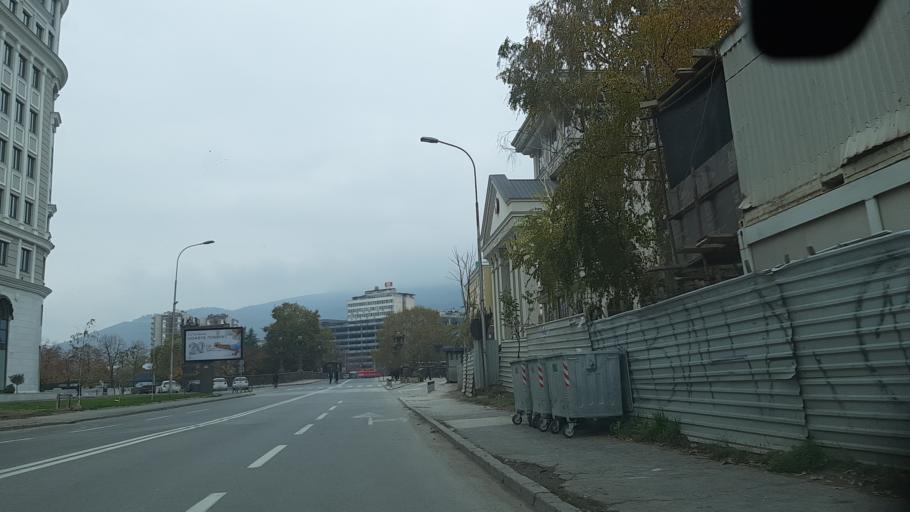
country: MK
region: Karpos
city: Skopje
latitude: 41.9964
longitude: 21.4378
